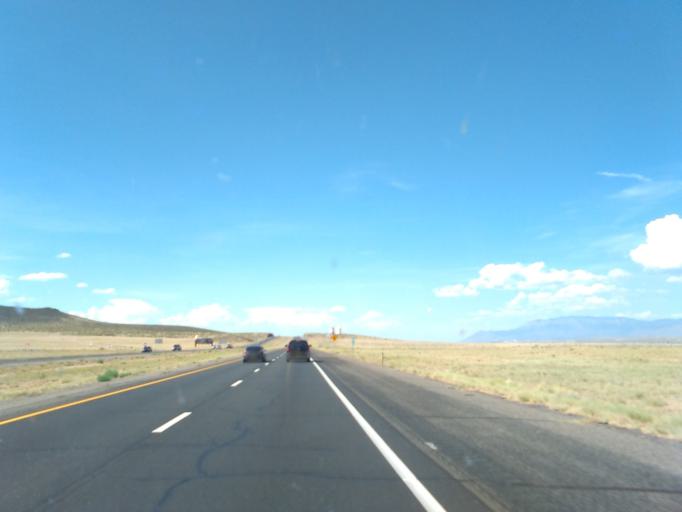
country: US
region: New Mexico
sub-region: Valencia County
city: Bosque Farms
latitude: 34.9054
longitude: -106.7237
